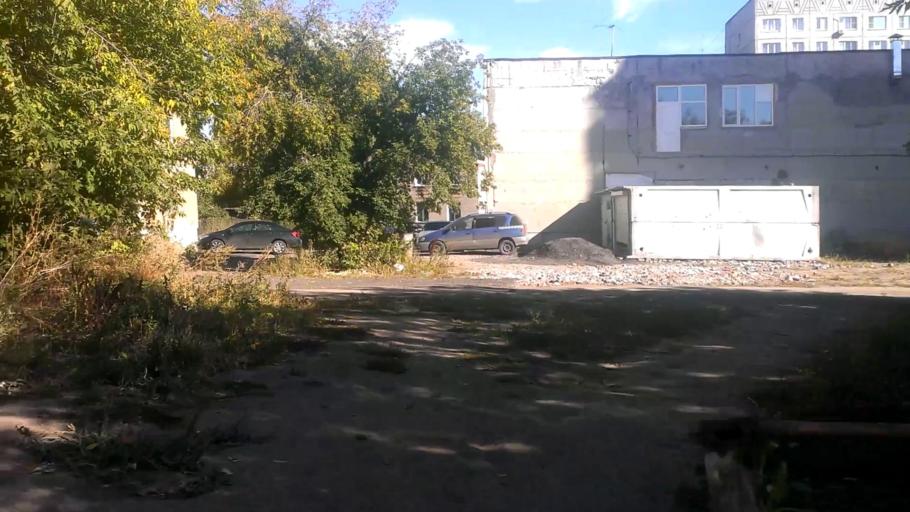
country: RU
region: Altai Krai
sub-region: Gorod Barnaulskiy
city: Barnaul
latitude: 53.3721
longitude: 83.6867
